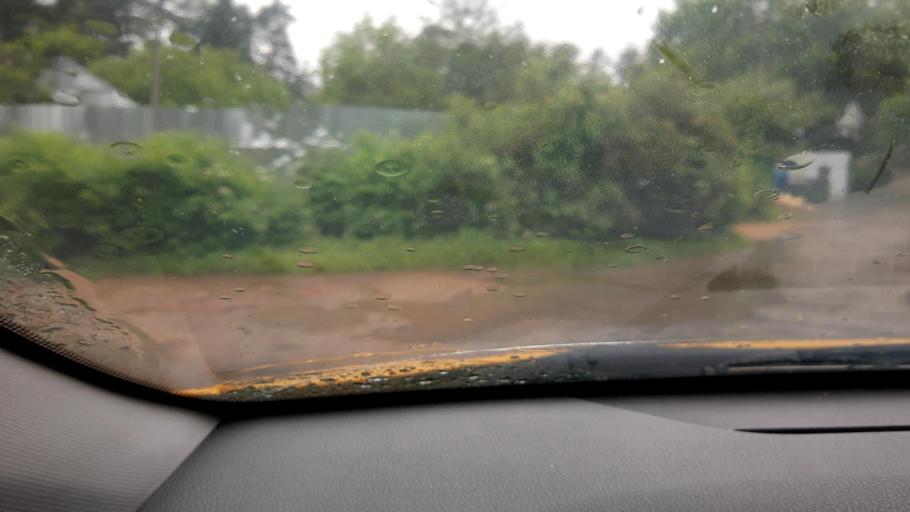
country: RU
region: Moskovskaya
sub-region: Podol'skiy Rayon
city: Podol'sk
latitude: 55.4102
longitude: 37.6119
